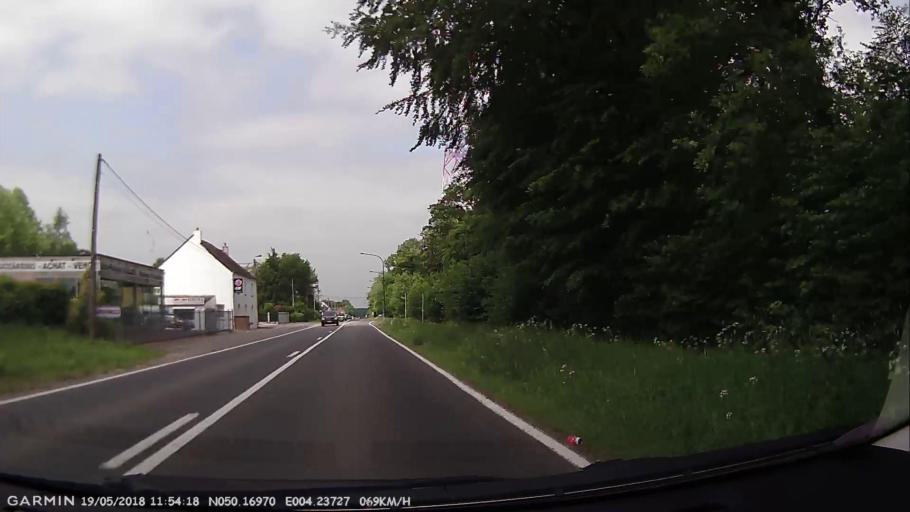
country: BE
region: Wallonia
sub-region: Province du Hainaut
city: Beaumont
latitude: 50.1698
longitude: 4.2372
